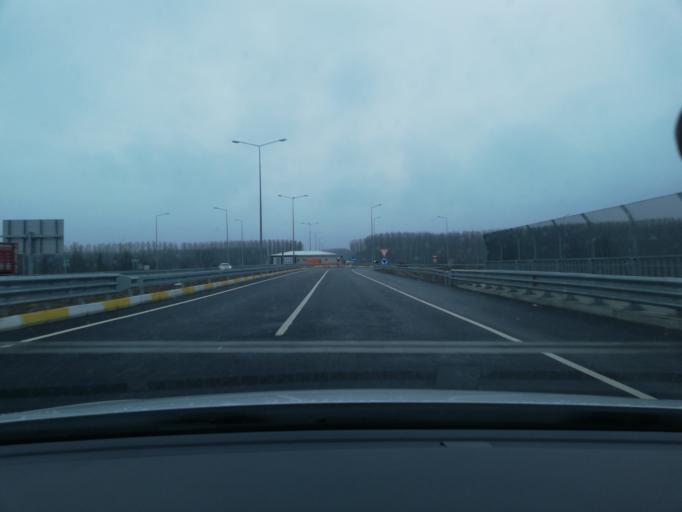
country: TR
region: Duzce
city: Duzce
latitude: 40.8043
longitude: 31.1684
